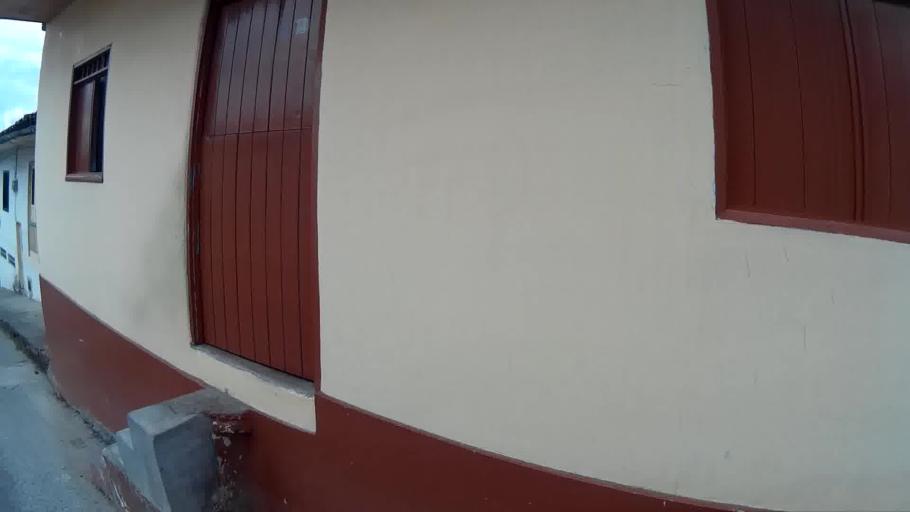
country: CO
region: Risaralda
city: Marsella
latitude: 4.9379
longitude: -75.7397
